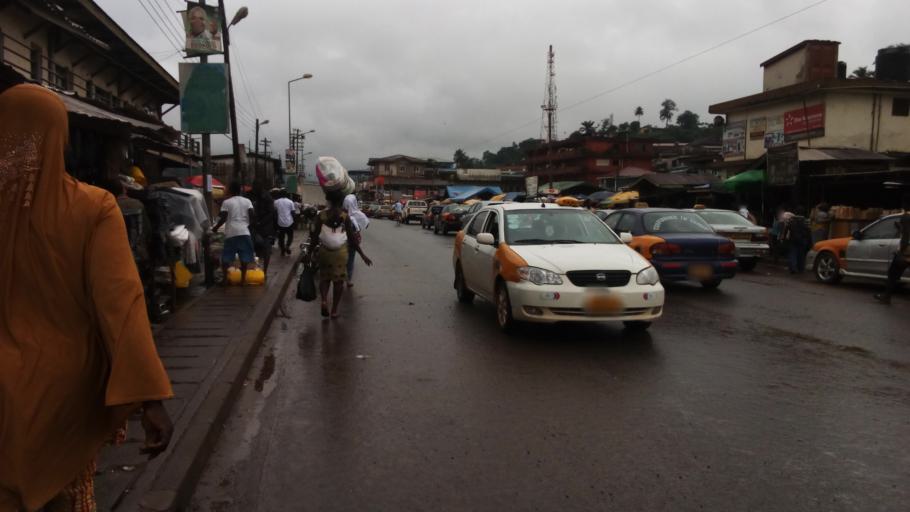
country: GH
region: Western
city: Tarkwa
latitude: 5.3046
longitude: -1.9958
